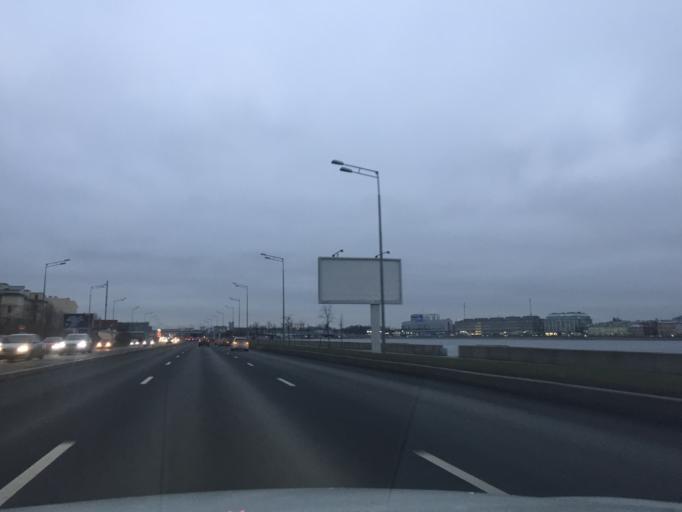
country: RU
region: St.-Petersburg
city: Centralniy
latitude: 59.9345
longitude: 30.4013
